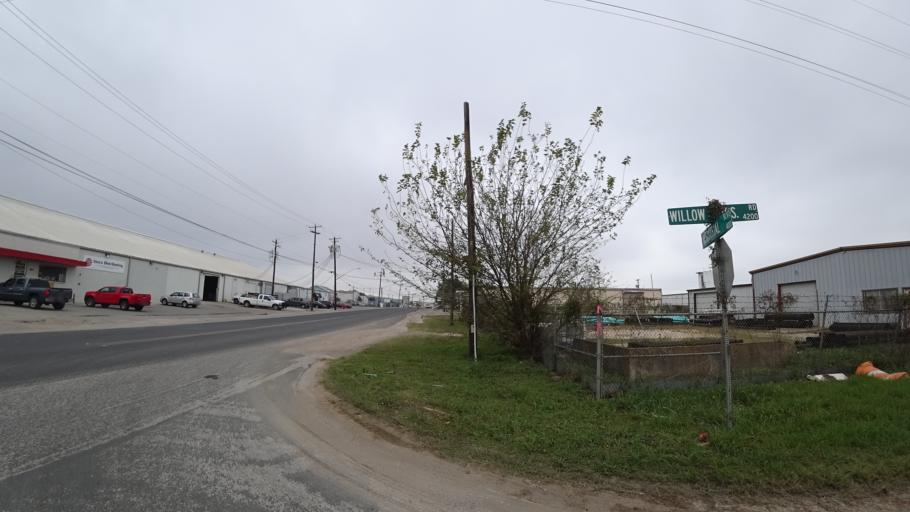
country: US
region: Texas
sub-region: Travis County
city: Austin
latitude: 30.2186
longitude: -97.7622
